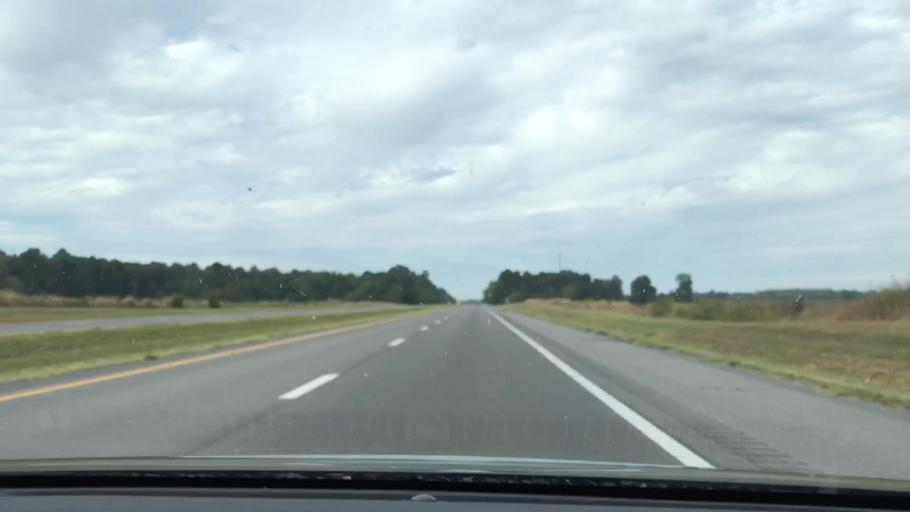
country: US
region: Kentucky
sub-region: Marshall County
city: Benton
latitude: 36.8271
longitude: -88.4594
